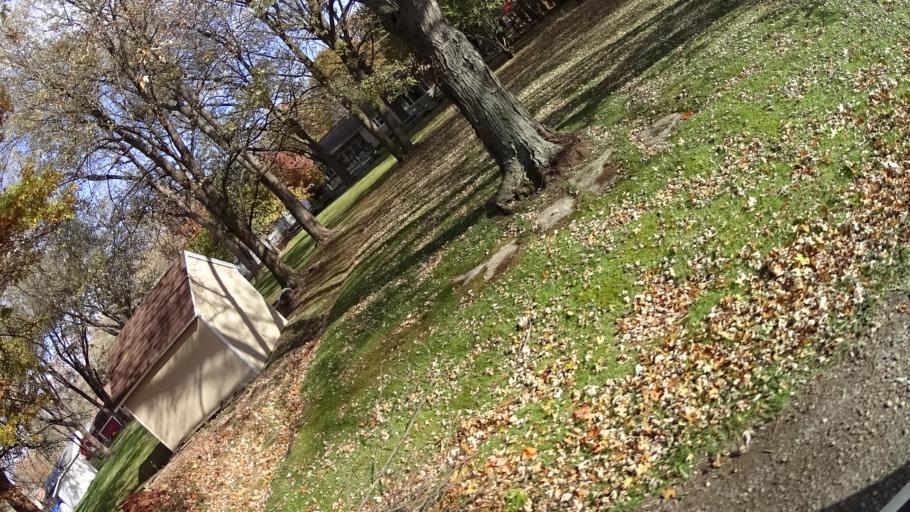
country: US
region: Ohio
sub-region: Lorain County
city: Avon Lake
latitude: 41.5046
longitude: -82.0385
